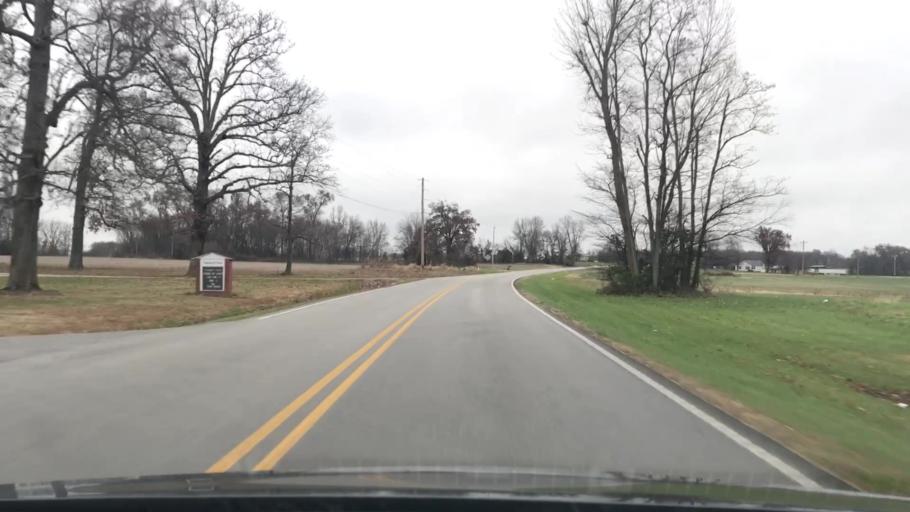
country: US
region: Kentucky
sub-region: Todd County
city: Guthrie
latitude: 36.7290
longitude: -87.1896
